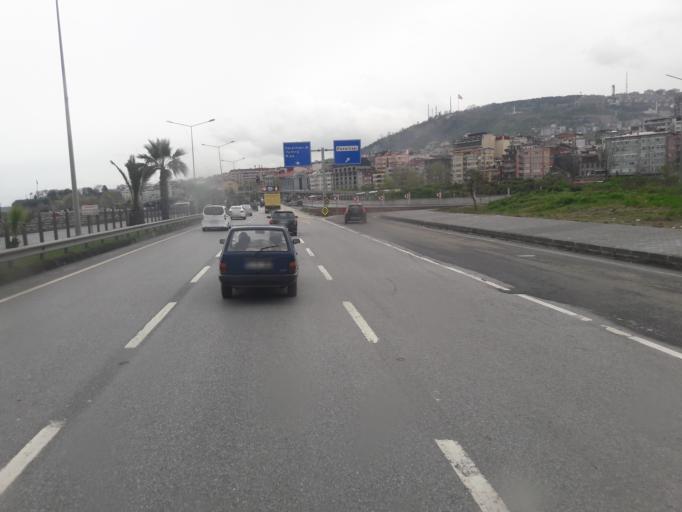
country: TR
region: Trabzon
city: Trabzon
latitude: 41.0111
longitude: 39.7237
